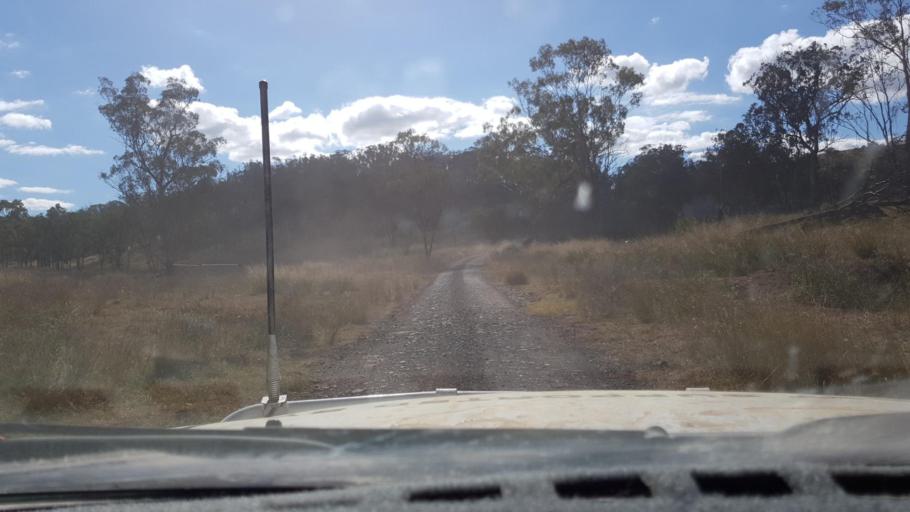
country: AU
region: New South Wales
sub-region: Tamworth Municipality
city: Manilla
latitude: -30.4773
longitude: 150.7727
